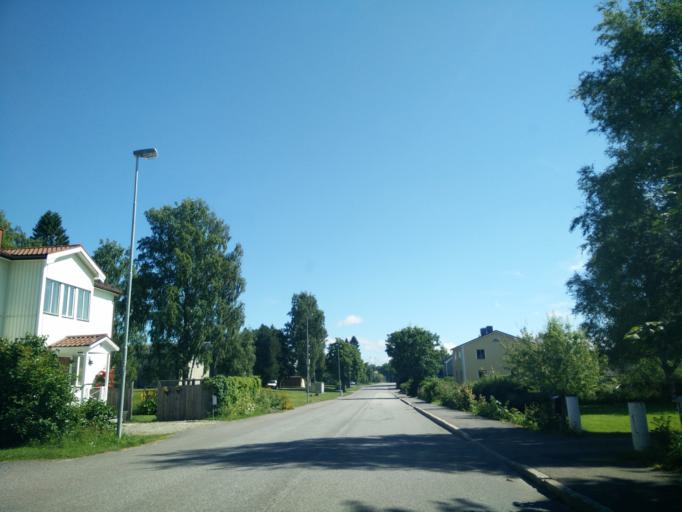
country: SE
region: Vaesternorrland
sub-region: Haernoesands Kommun
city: Haernoesand
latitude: 62.6317
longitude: 17.9083
